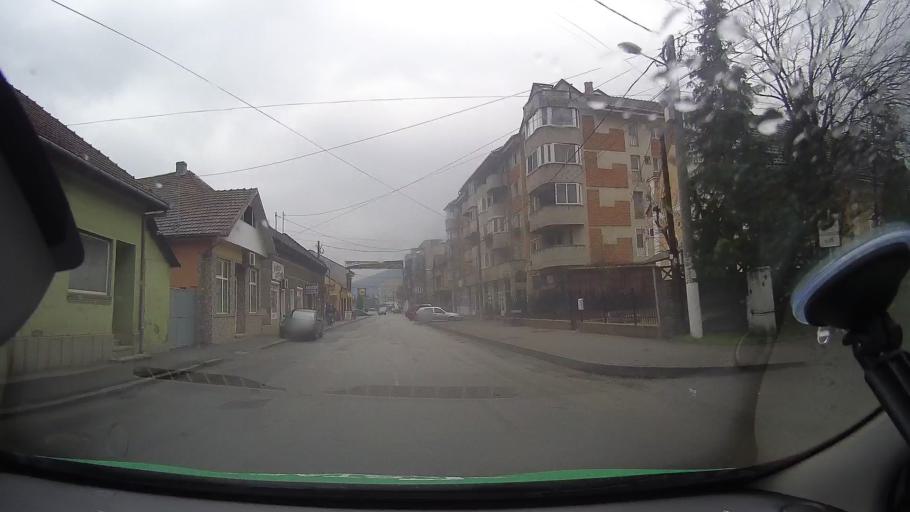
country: RO
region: Hunedoara
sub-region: Municipiul Brad
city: Brad
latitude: 46.1328
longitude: 22.7875
